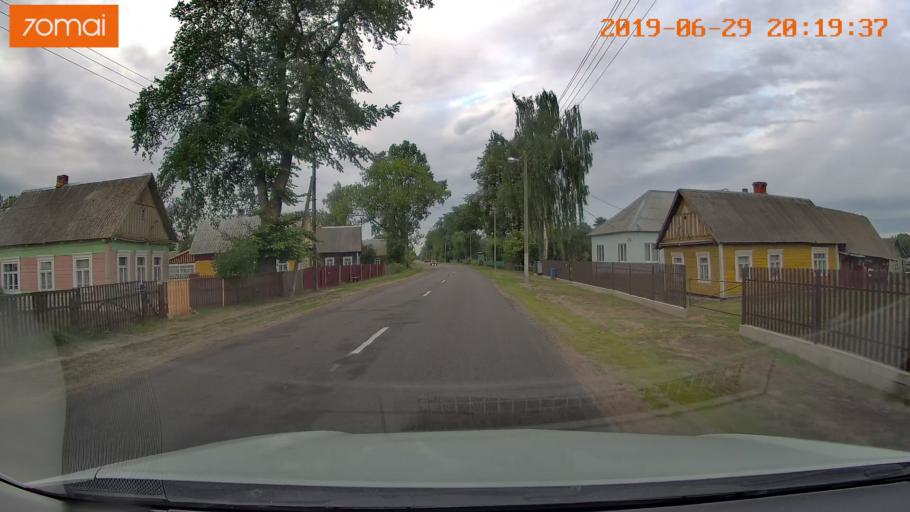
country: BY
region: Brest
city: Asnyezhytsy
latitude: 52.4029
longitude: 26.2452
